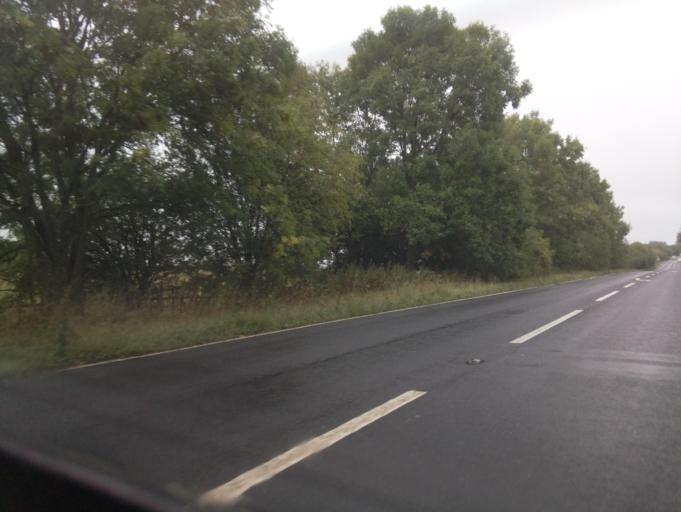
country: GB
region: England
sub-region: North Yorkshire
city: Pannal
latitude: 53.9321
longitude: -1.5374
